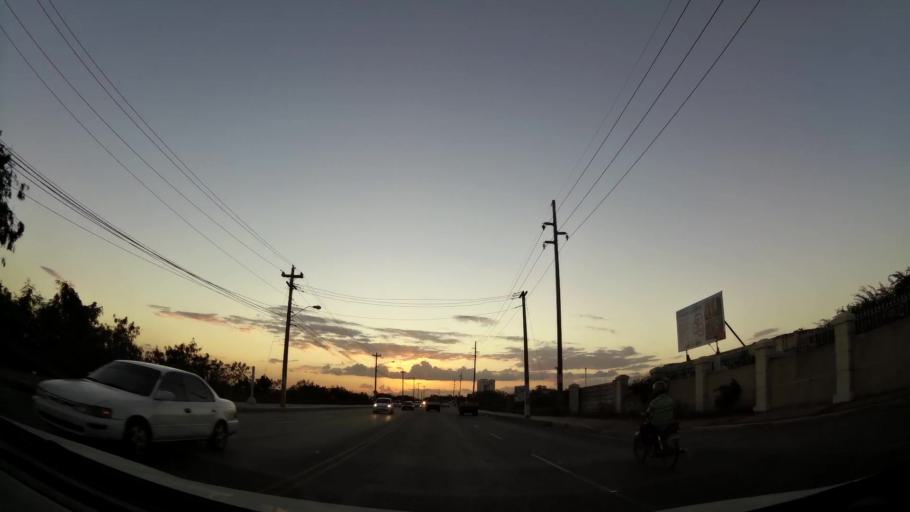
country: DO
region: Santo Domingo
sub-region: Santo Domingo
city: Santo Domingo Este
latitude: 18.4840
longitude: -69.8359
